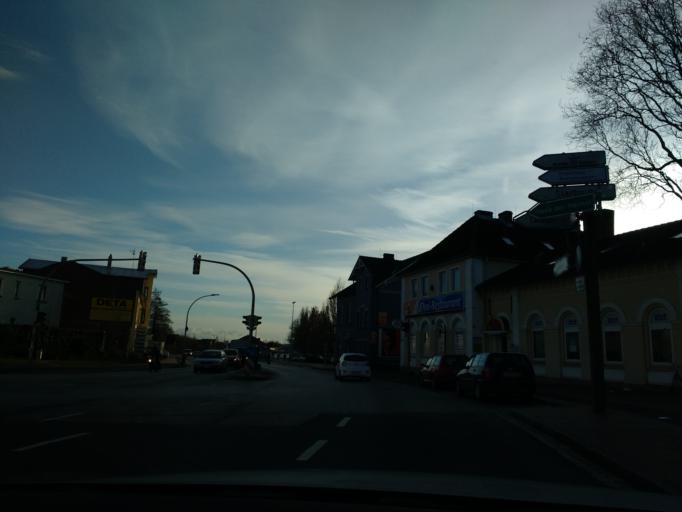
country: DE
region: Schleswig-Holstein
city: Itzehoe
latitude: 53.9243
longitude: 9.5110
